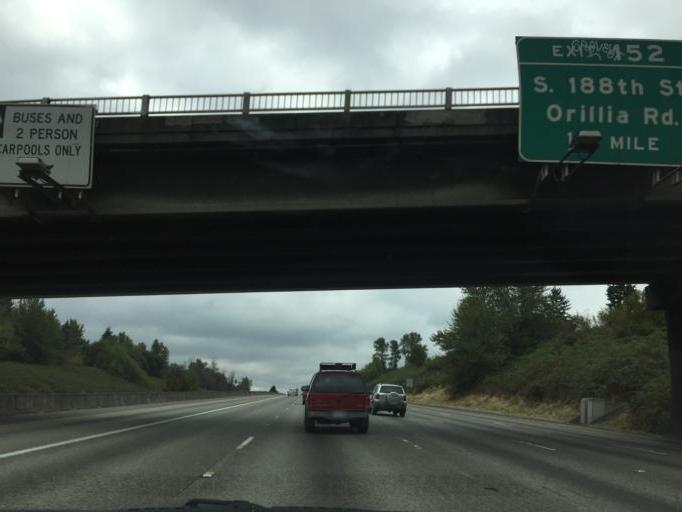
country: US
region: Washington
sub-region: King County
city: SeaTac
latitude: 47.4440
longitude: -122.2681
